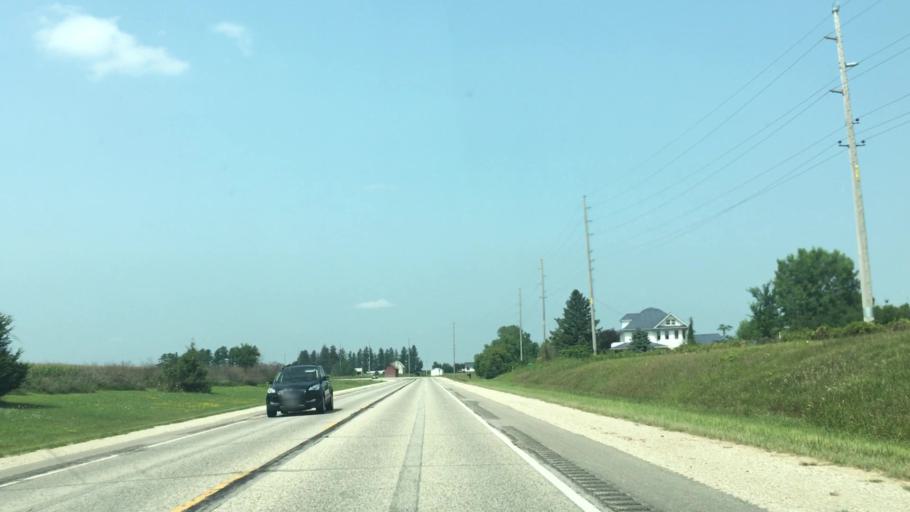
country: US
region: Iowa
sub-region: Fayette County
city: Fayette
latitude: 42.9013
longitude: -91.8105
